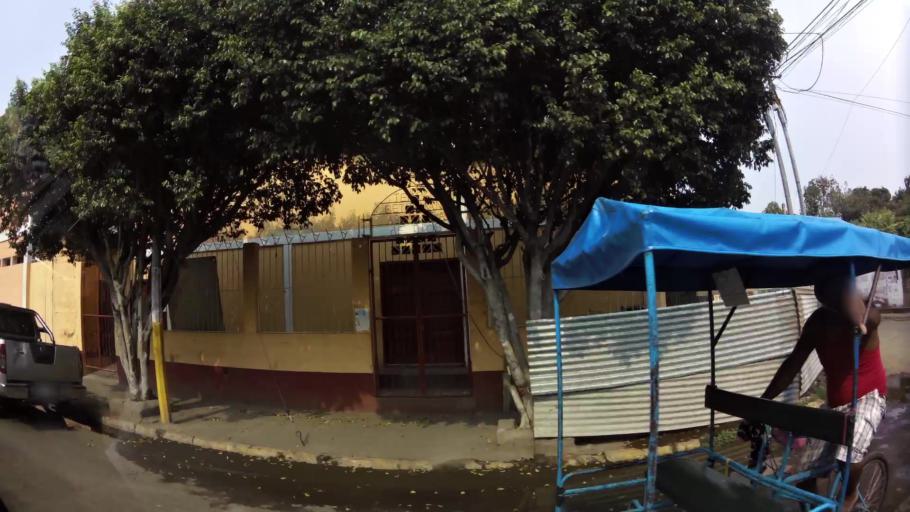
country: NI
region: Chinandega
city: Chinandega
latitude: 12.6250
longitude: -87.1325
